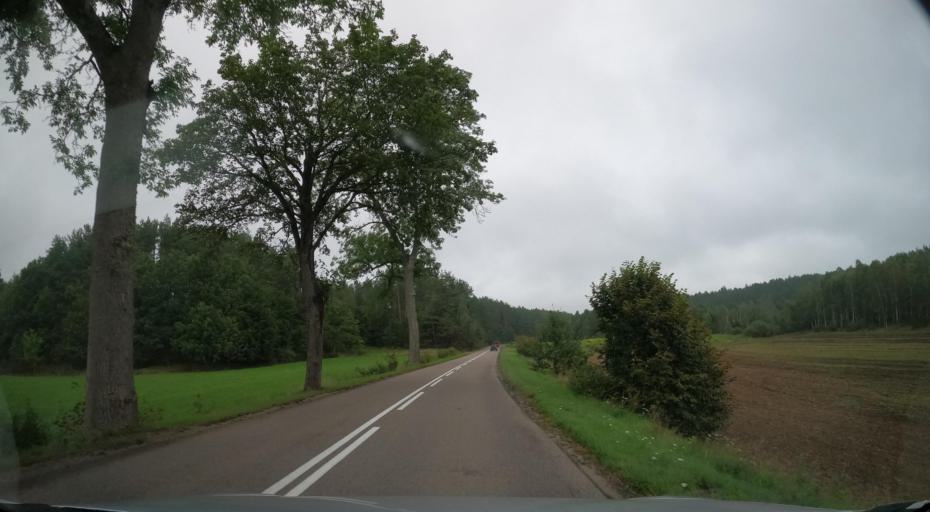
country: PL
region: Pomeranian Voivodeship
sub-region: Powiat wejherowski
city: Luzino
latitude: 54.4732
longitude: 18.0814
